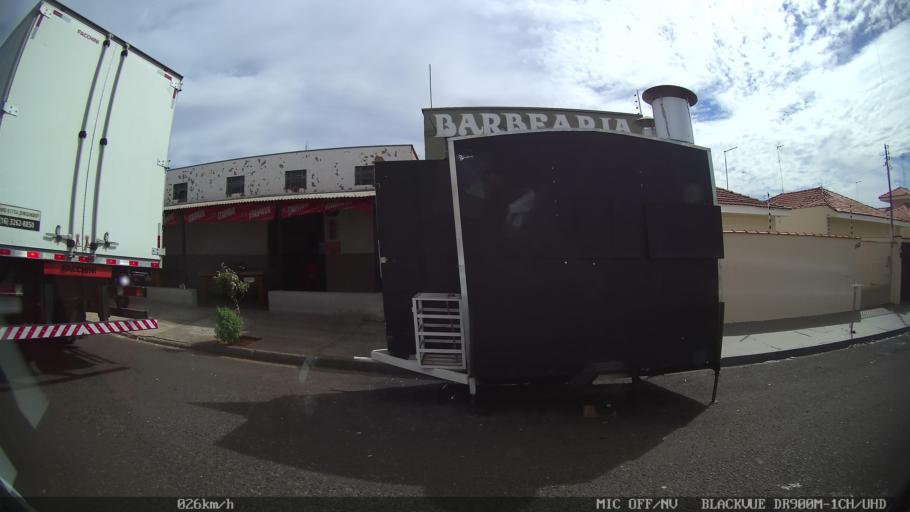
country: BR
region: Sao Paulo
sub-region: Catanduva
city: Catanduva
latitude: -21.1563
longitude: -48.9771
